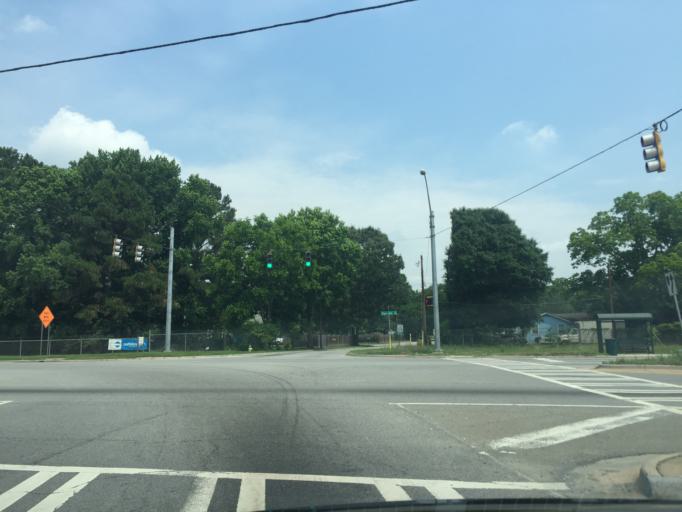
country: US
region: Georgia
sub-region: Chatham County
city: Savannah
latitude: 32.0544
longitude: -81.1388
